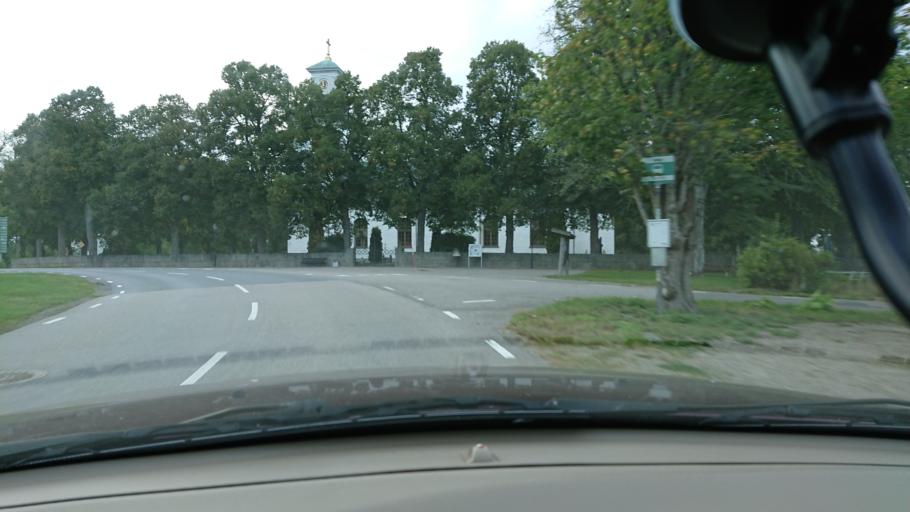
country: SE
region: Kronoberg
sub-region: Vaxjo Kommun
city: Lammhult
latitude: 57.0827
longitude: 14.7093
